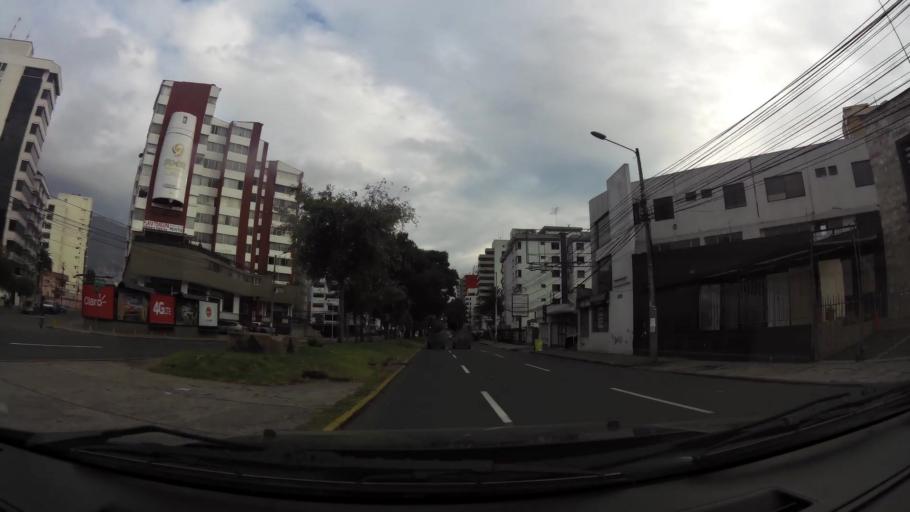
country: EC
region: Pichincha
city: Quito
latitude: -0.1965
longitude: -78.4835
